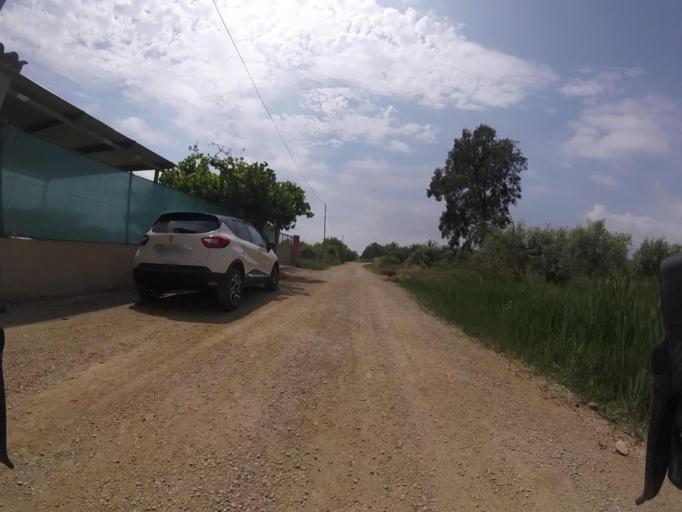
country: ES
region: Valencia
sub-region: Provincia de Castello
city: Orpesa/Oropesa del Mar
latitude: 40.1480
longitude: 0.1656
